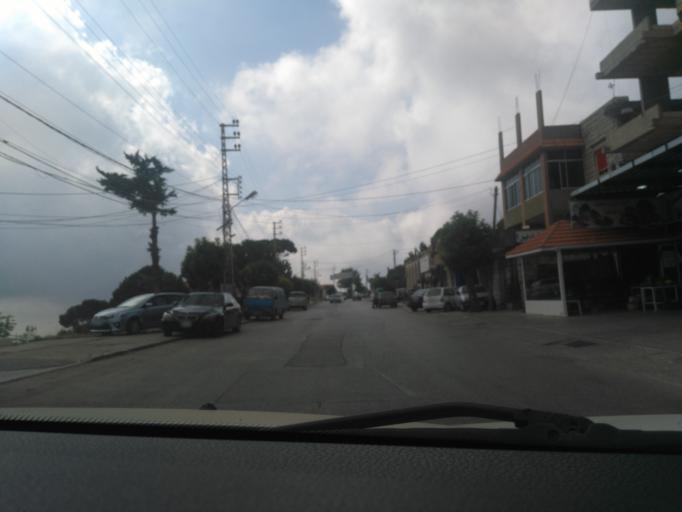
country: LB
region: Mont-Liban
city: Bhamdoun el Mhatta
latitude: 33.8499
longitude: 35.7270
